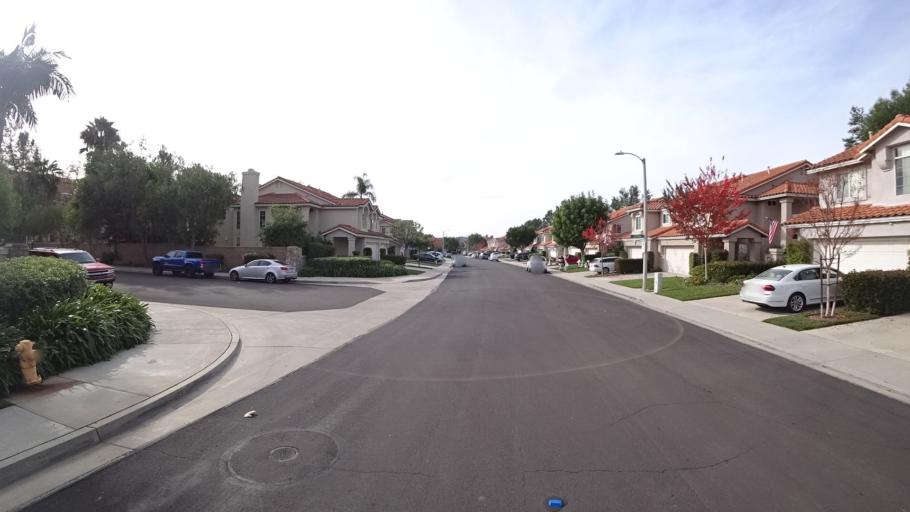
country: US
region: California
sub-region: Orange County
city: Laguna Woods
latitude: 33.6083
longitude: -117.7347
